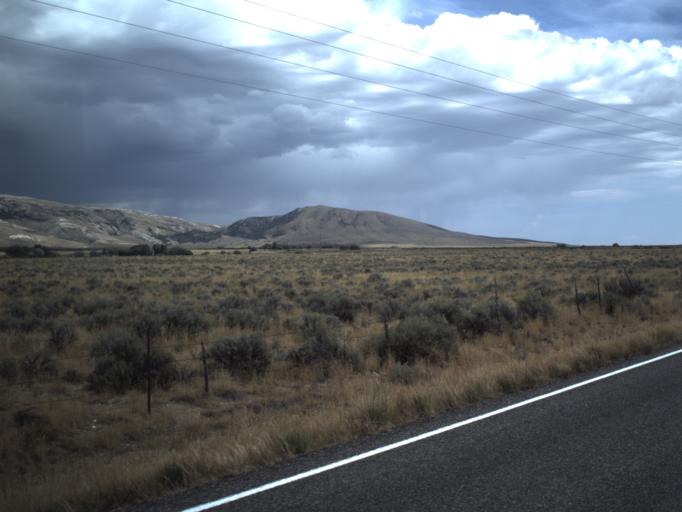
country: US
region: Idaho
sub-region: Cassia County
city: Burley
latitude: 41.8166
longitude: -113.3590
